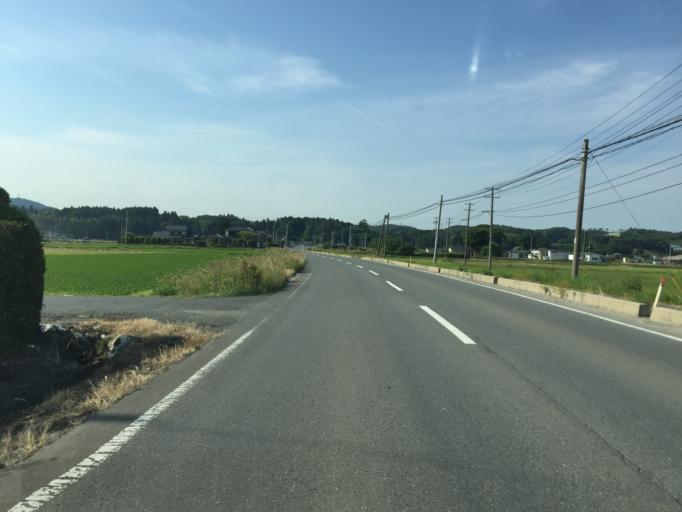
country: JP
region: Fukushima
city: Namie
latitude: 37.6645
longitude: 140.9327
